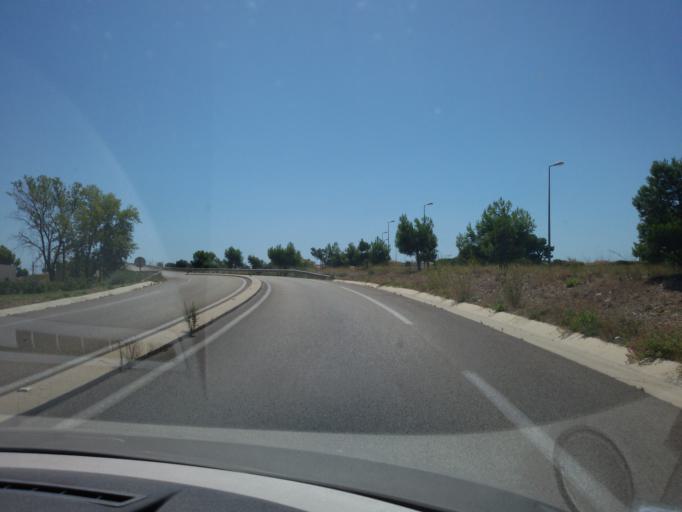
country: FR
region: Languedoc-Roussillon
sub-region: Departement de l'Herault
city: Frontignan
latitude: 43.4651
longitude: 3.7665
